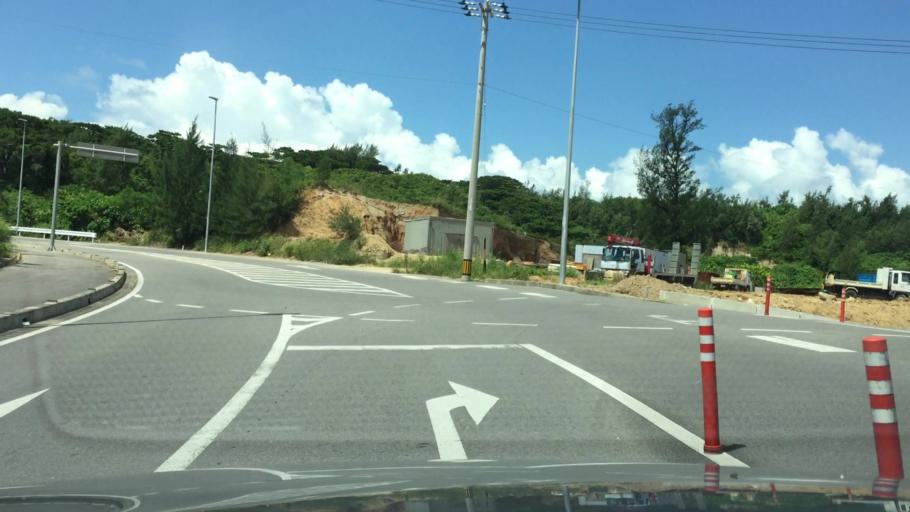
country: JP
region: Okinawa
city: Ishigaki
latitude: 24.3772
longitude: 124.1274
